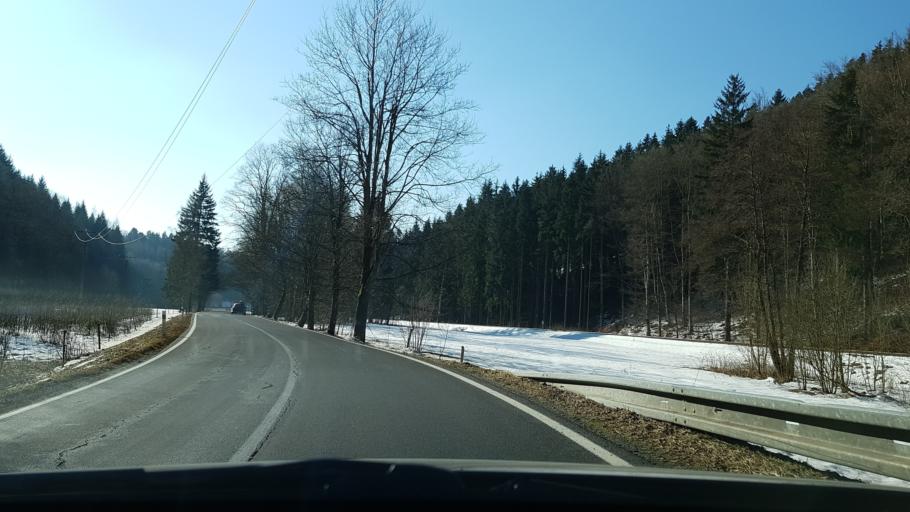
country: CZ
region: Olomoucky
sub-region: Okres Sumperk
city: Stare Mesto
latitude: 50.1244
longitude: 17.0078
